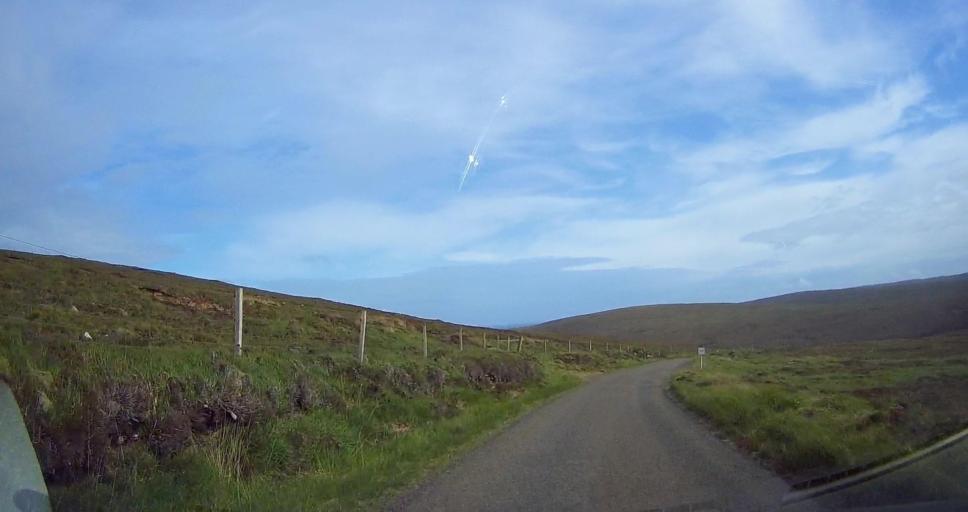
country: GB
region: Scotland
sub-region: Orkney Islands
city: Stromness
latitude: 58.8788
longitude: -3.2481
